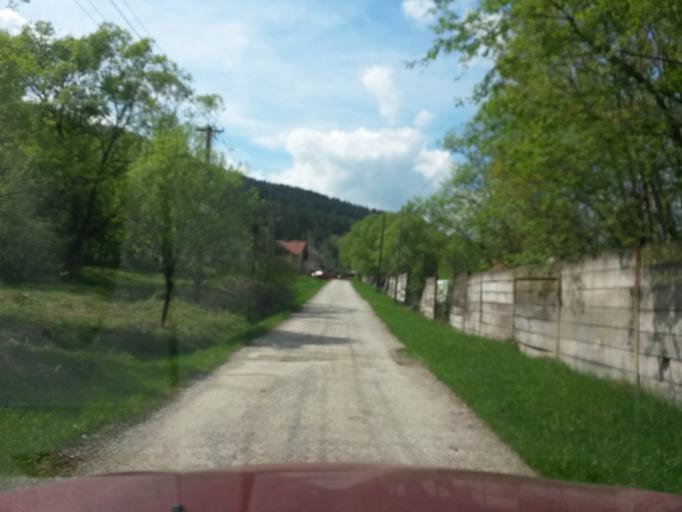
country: SK
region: Kosicky
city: Gelnica
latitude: 48.8157
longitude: 20.8891
